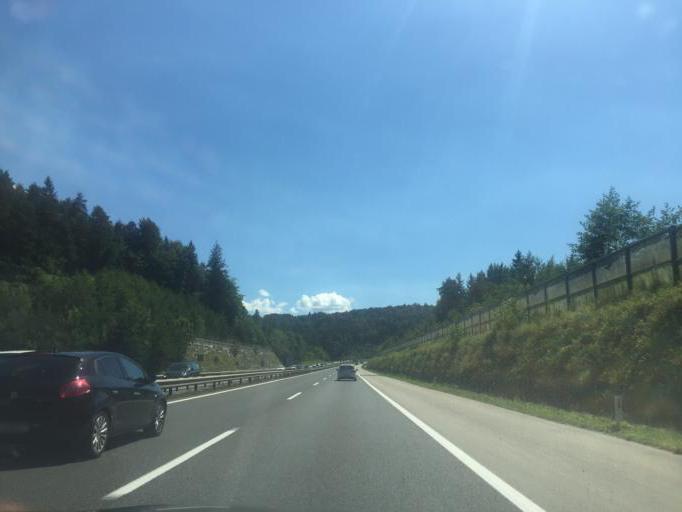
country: SI
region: Skofljica
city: Lavrica
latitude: 46.0288
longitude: 14.5684
